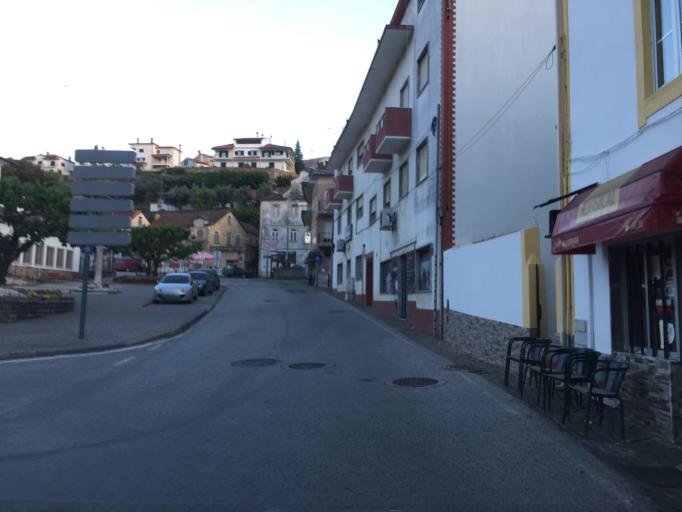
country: PT
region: Coimbra
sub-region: Pampilhosa da Serra
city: Pampilhosa da Serra
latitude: 40.0466
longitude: -7.9509
